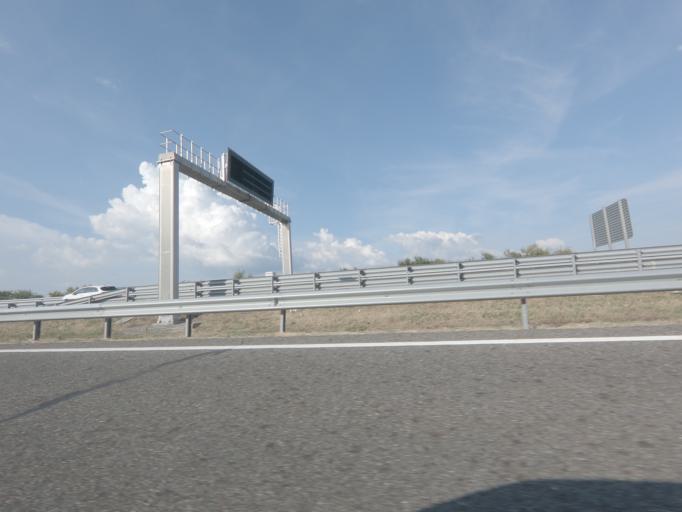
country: ES
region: Galicia
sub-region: Provincia de Ourense
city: Cualedro
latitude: 41.9738
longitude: -7.5310
